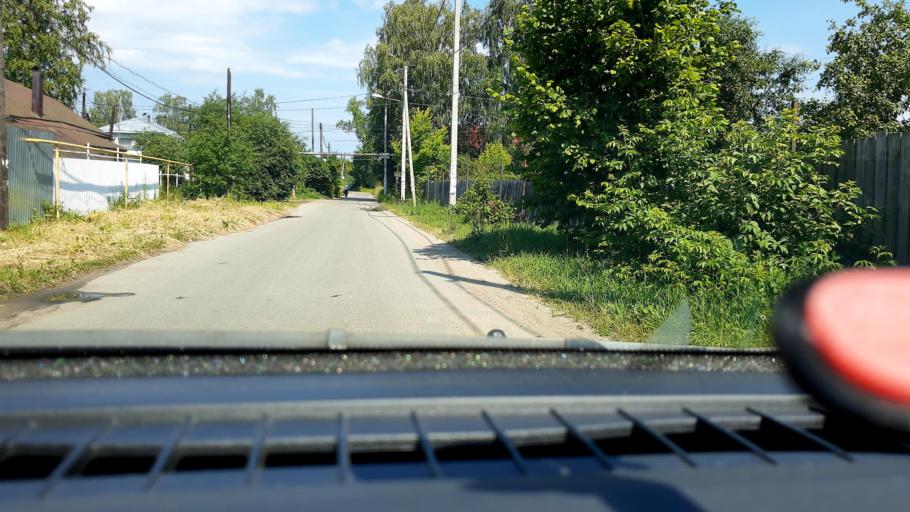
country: RU
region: Nizjnij Novgorod
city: Burevestnik
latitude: 56.2022
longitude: 43.7930
